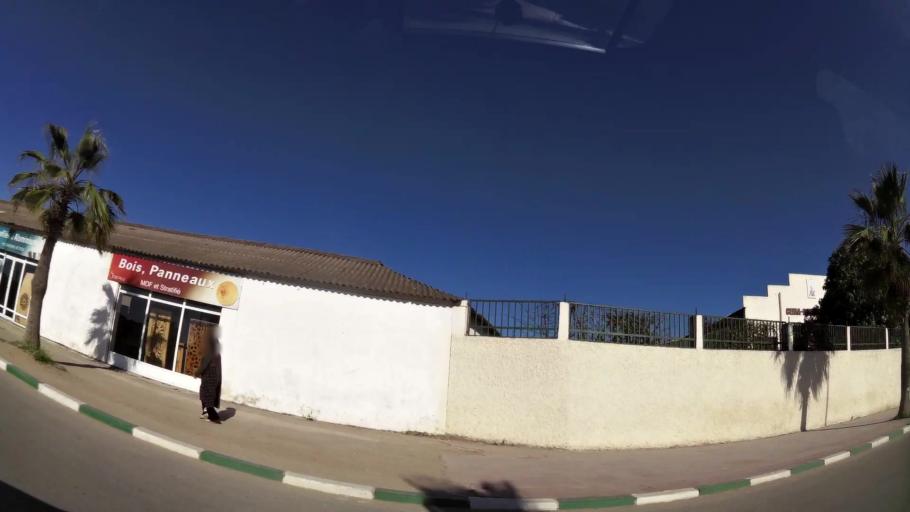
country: MA
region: Meknes-Tafilalet
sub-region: Meknes
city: Meknes
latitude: 33.8751
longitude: -5.5744
